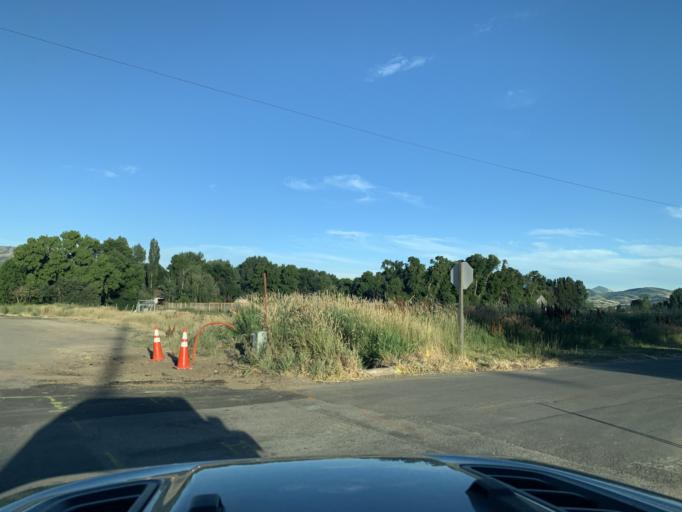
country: US
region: Utah
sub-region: Weber County
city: Wolf Creek
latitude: 41.2988
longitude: -111.8129
